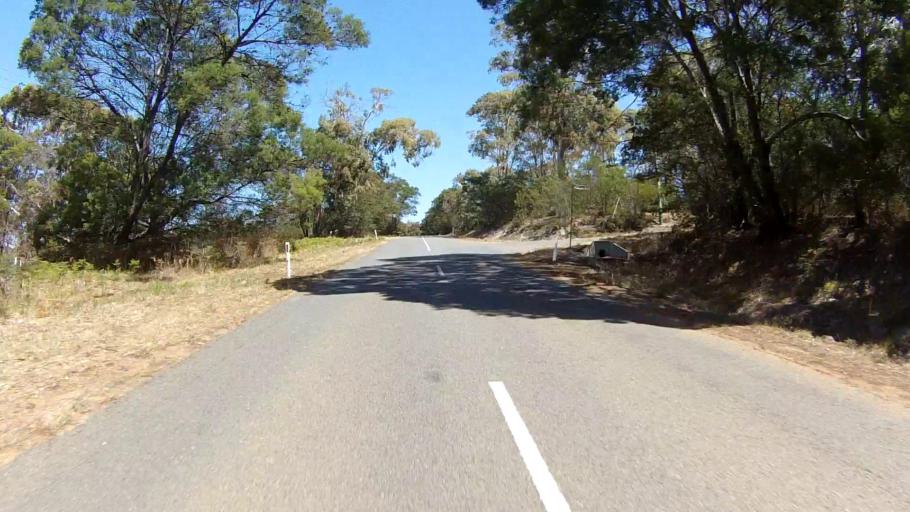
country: AU
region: Tasmania
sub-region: Clarence
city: Sandford
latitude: -42.9914
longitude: 147.4783
